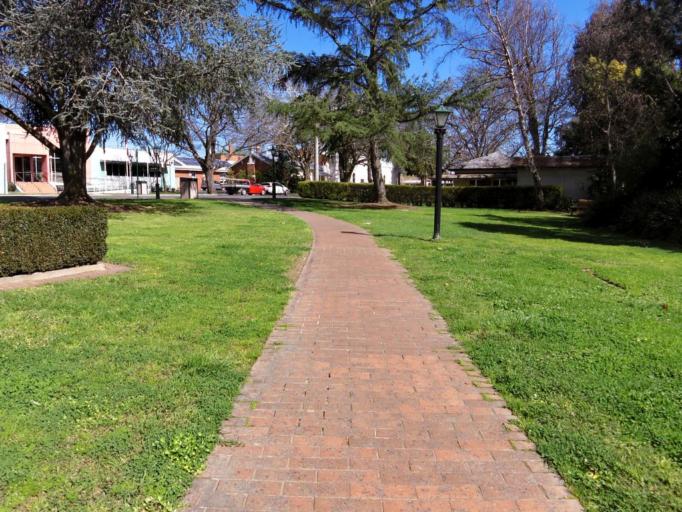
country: AU
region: Victoria
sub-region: Murrindindi
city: Alexandra
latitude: -37.1902
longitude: 145.7103
